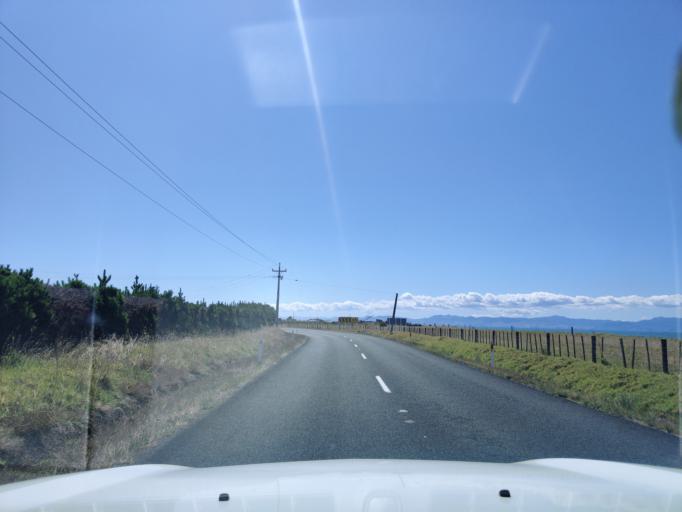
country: NZ
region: Waikato
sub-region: Thames-Coromandel District
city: Thames
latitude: -37.0651
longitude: 175.2981
